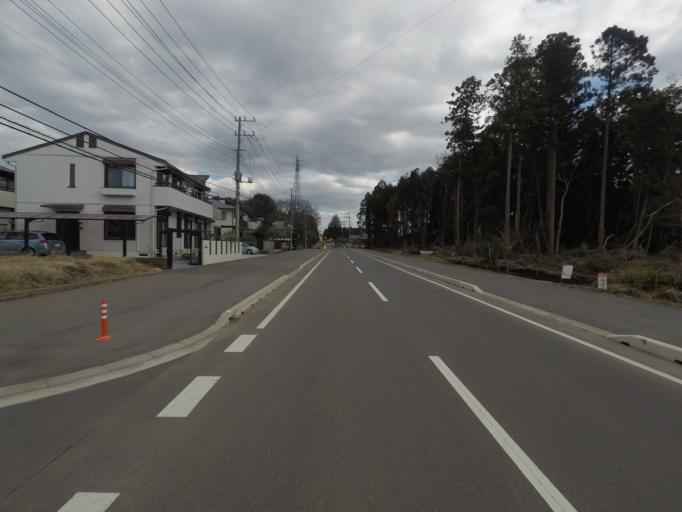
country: JP
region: Ibaraki
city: Naka
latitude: 36.0307
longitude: 140.1209
